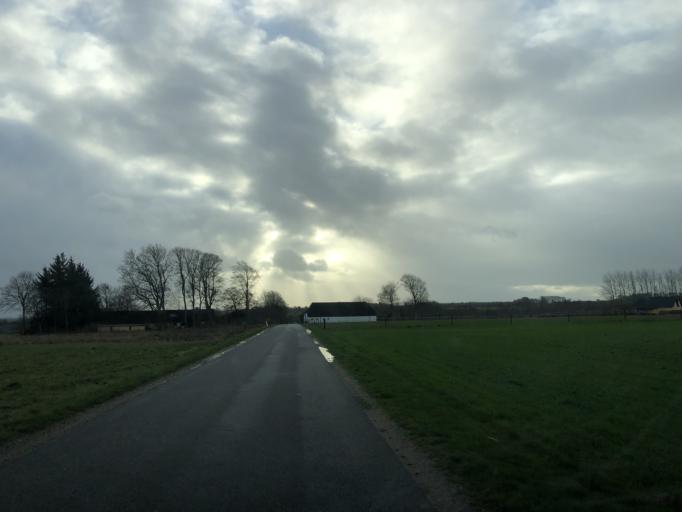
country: DK
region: North Denmark
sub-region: Rebild Kommune
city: Stovring
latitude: 56.8980
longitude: 9.7819
